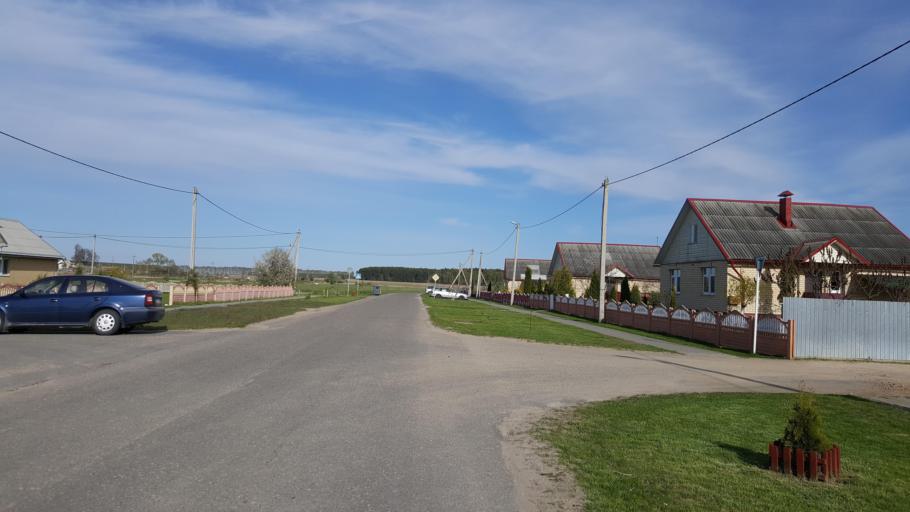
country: BY
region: Brest
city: Vysokaye
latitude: 52.4114
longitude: 23.4618
